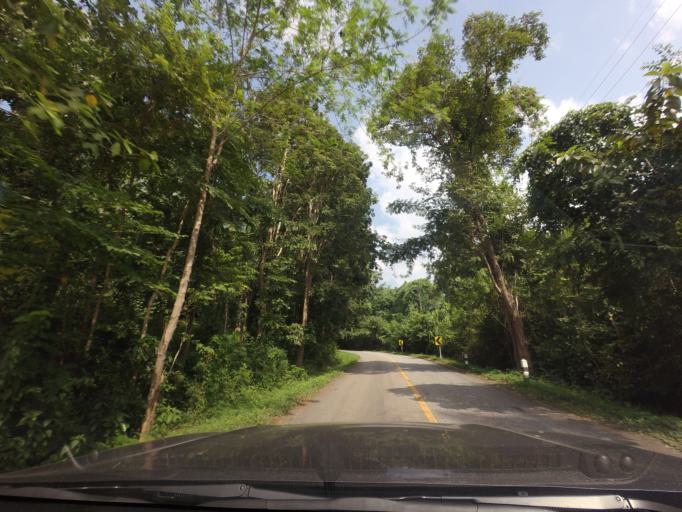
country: TH
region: Phitsanulok
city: Nakhon Thai
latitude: 17.0224
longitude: 100.9392
